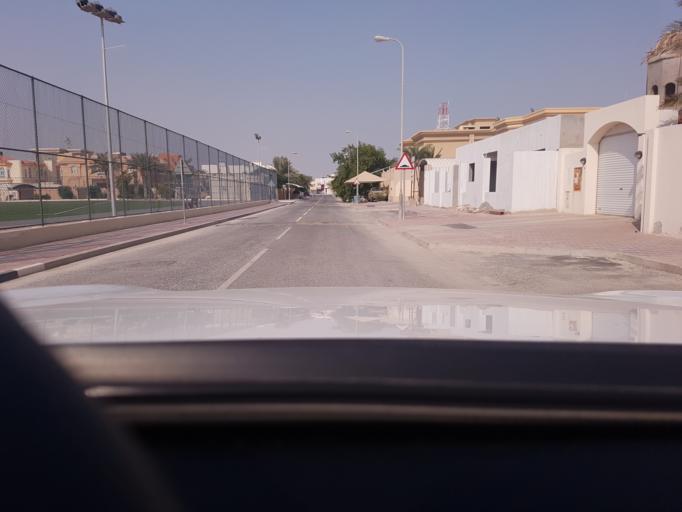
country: QA
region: Baladiyat ad Dawhah
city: Doha
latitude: 25.2343
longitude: 51.5596
